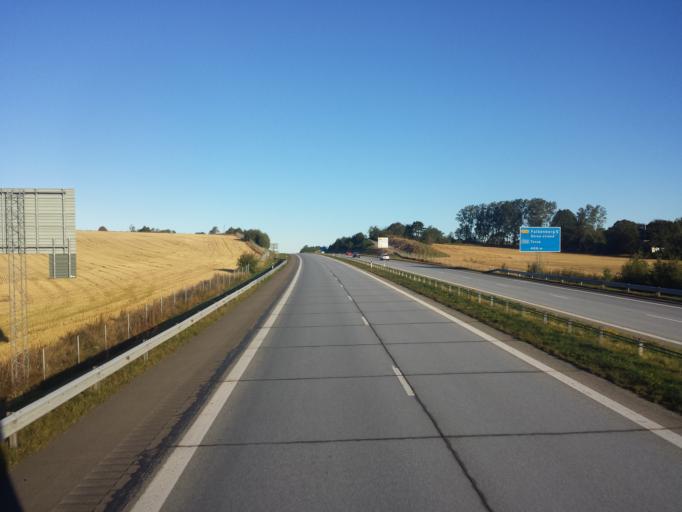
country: SE
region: Halland
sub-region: Falkenbergs Kommun
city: Falkenberg
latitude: 56.8956
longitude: 12.5918
